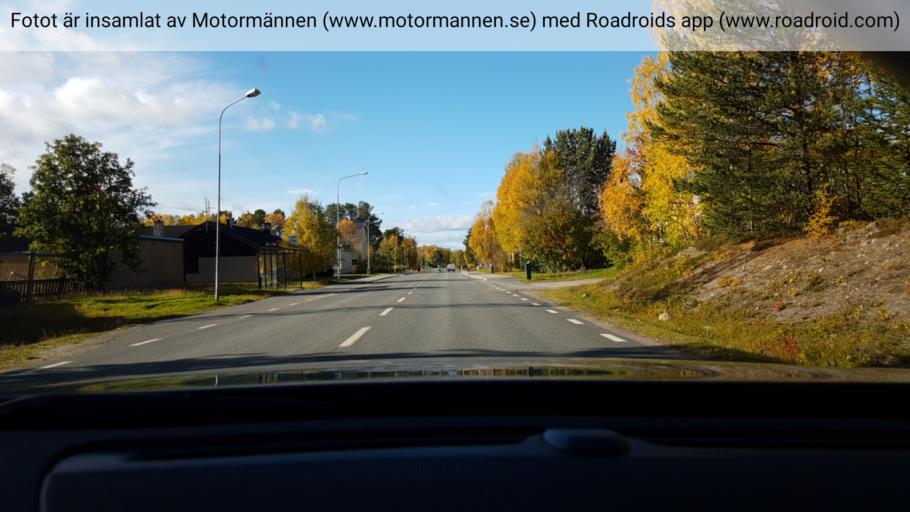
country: SE
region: Norrbotten
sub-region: Arjeplogs Kommun
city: Arjeplog
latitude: 66.0512
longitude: 17.9025
